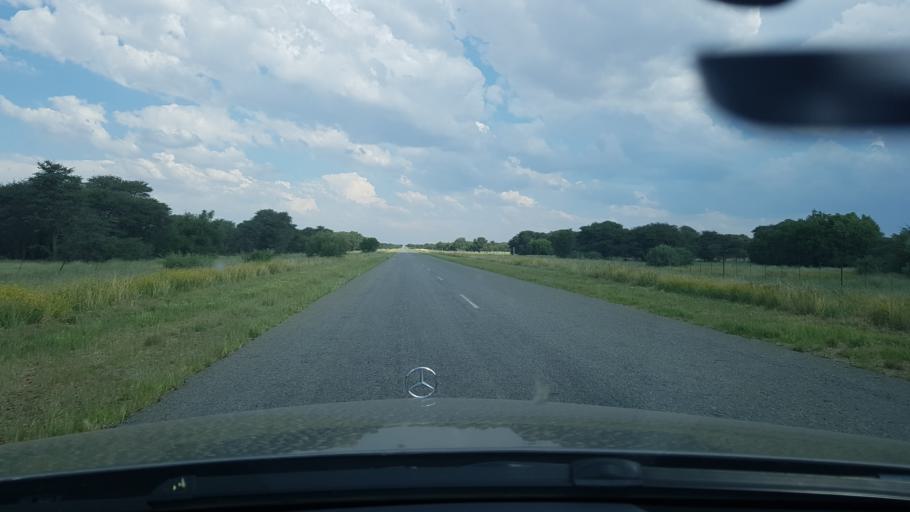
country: ZA
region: North-West
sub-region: Dr Ruth Segomotsi Mompati District Municipality
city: Bloemhof
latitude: -27.7751
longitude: 25.6059
